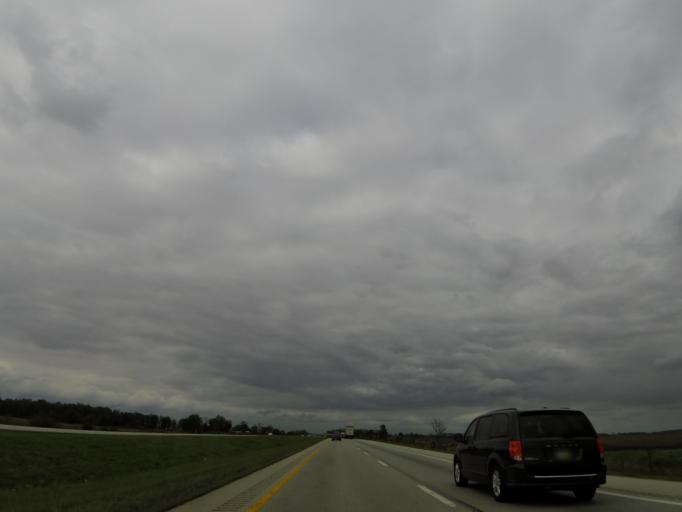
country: US
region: Ohio
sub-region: Clinton County
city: Wilmington
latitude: 39.5313
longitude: -83.8020
